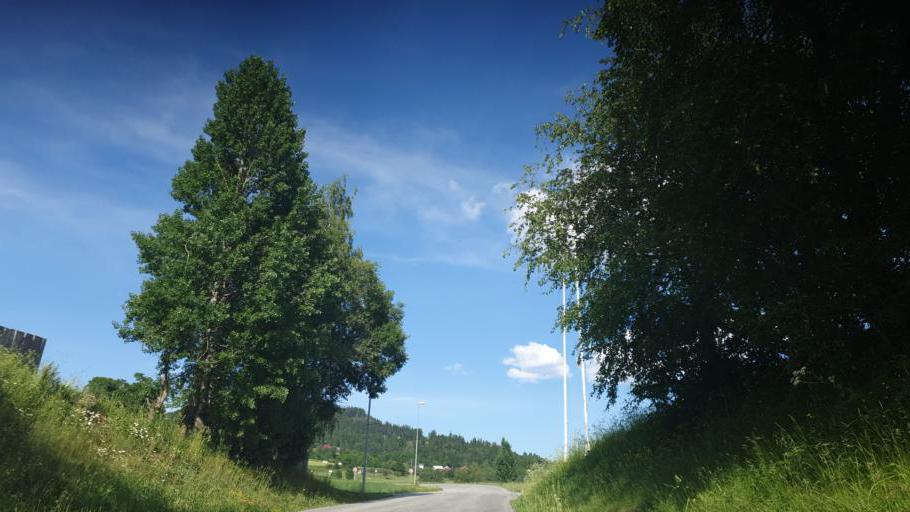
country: NO
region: Nord-Trondelag
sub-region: Leksvik
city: Leksvik
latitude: 63.6743
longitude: 10.6309
